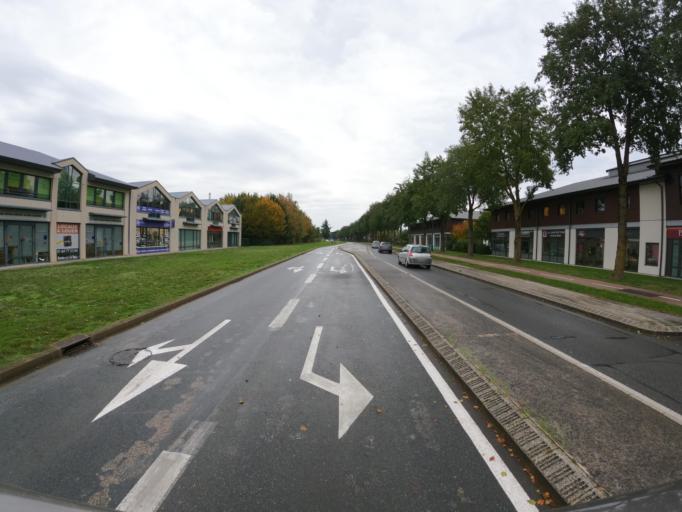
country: FR
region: Ile-de-France
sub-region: Departement de Seine-et-Marne
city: Serris
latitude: 48.8412
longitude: 2.7910
